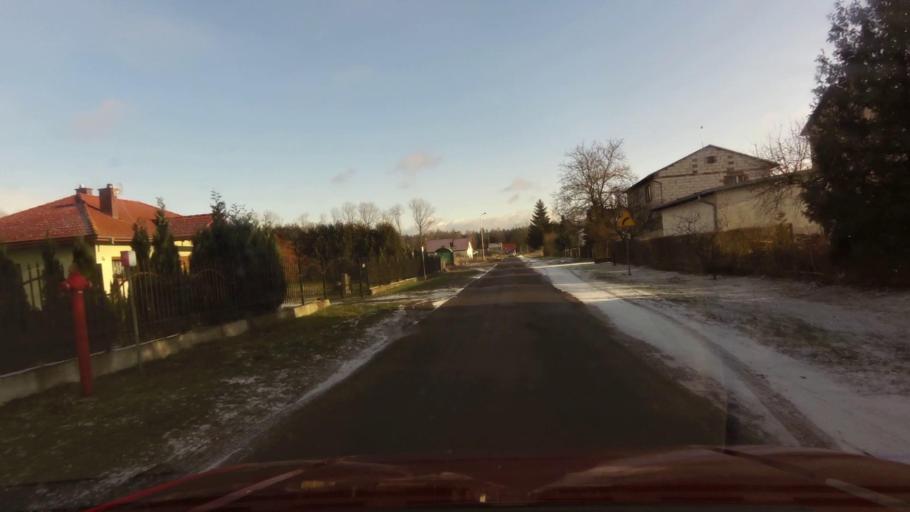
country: PL
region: West Pomeranian Voivodeship
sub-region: Powiat bialogardzki
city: Bialogard
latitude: 54.0921
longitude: 16.0657
